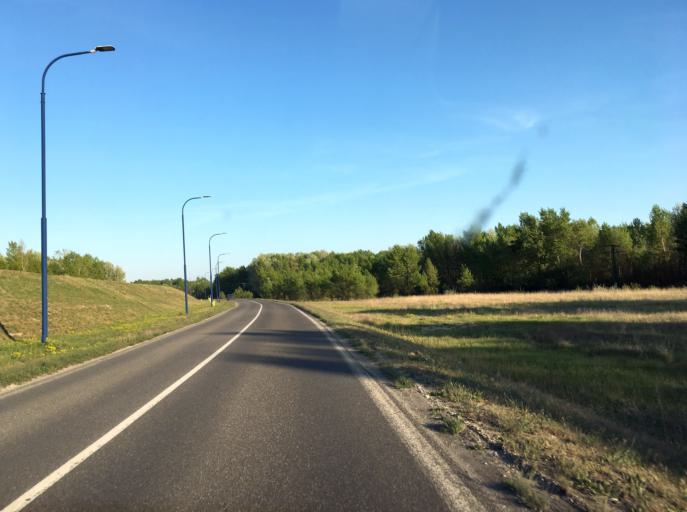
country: HU
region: Gyor-Moson-Sopron
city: Rajka
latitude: 48.0264
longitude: 17.2080
